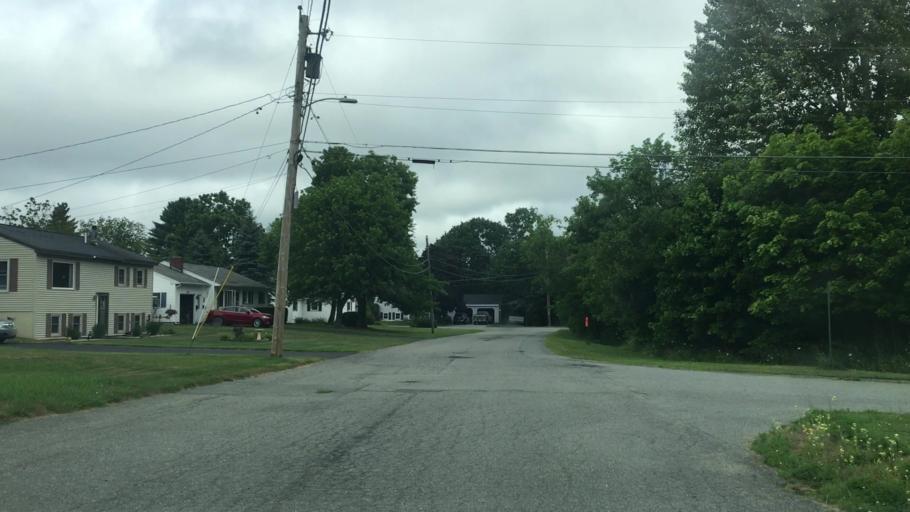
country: US
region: Maine
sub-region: Penobscot County
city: Brewer
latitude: 44.7733
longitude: -68.7695
